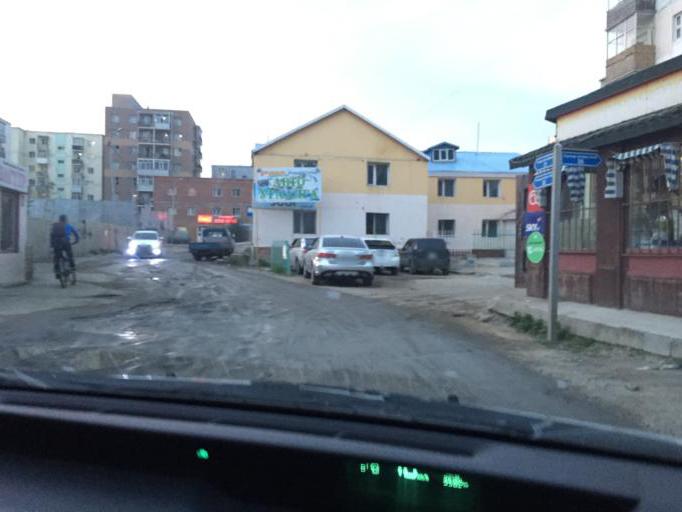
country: MN
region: Ulaanbaatar
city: Ulaanbaatar
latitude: 47.9242
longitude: 106.9499
